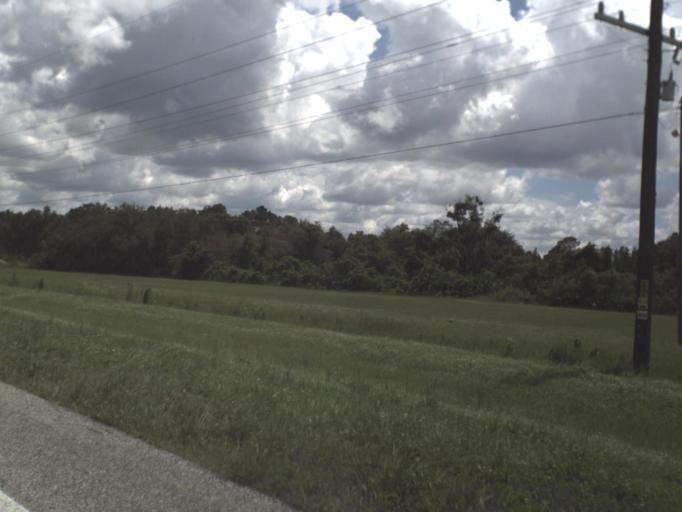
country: US
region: Florida
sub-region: Polk County
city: Babson Park
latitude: 27.8081
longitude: -81.3194
